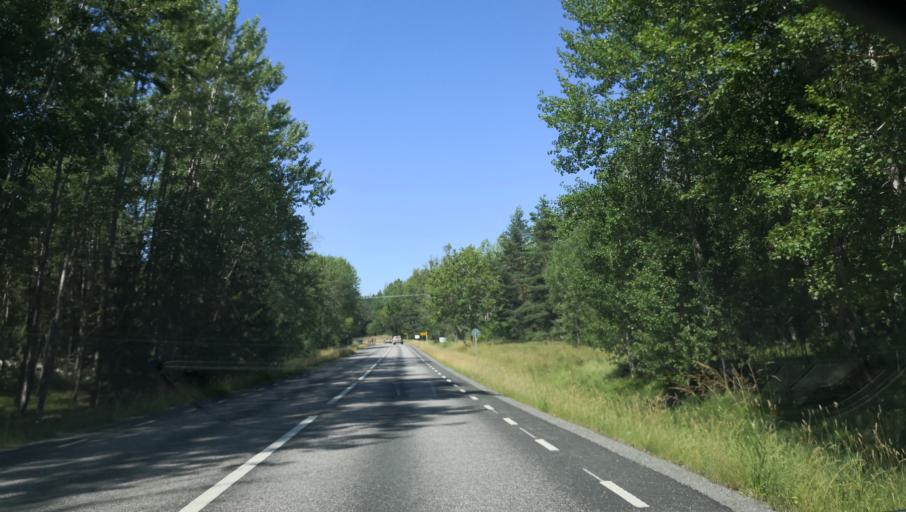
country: SE
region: Stockholm
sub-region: Varmdo Kommun
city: Mortnas
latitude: 59.3956
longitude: 18.4606
